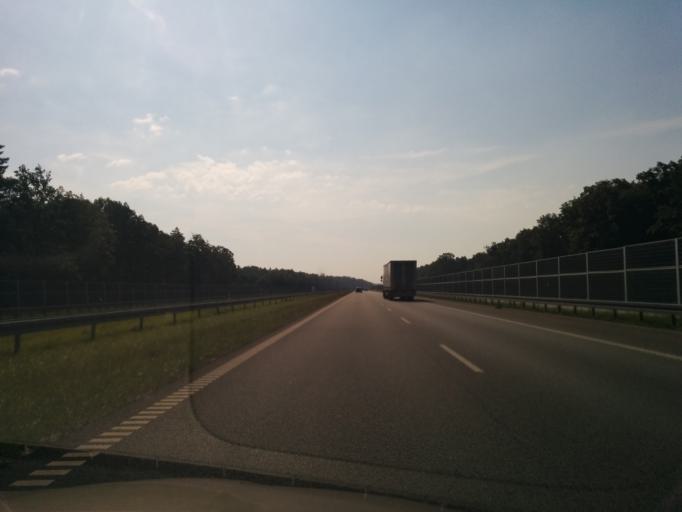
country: PL
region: Silesian Voivodeship
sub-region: Powiat tarnogorski
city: Radzionkow
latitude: 50.3835
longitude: 18.8583
